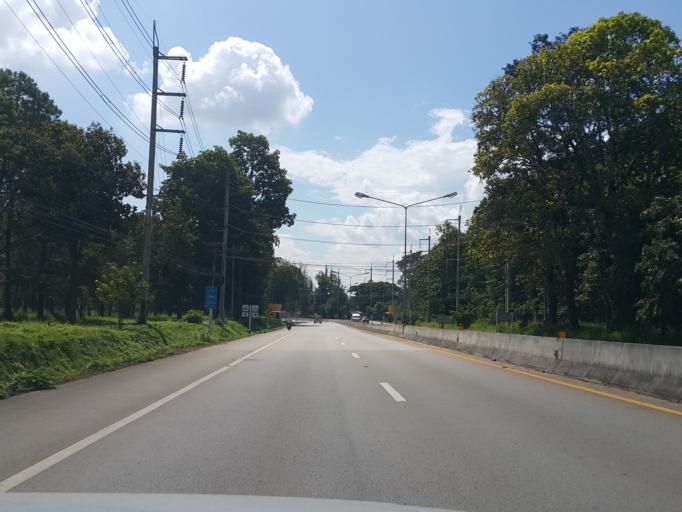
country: TH
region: Chiang Mai
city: Mae Taeng
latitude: 19.1489
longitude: 98.9473
